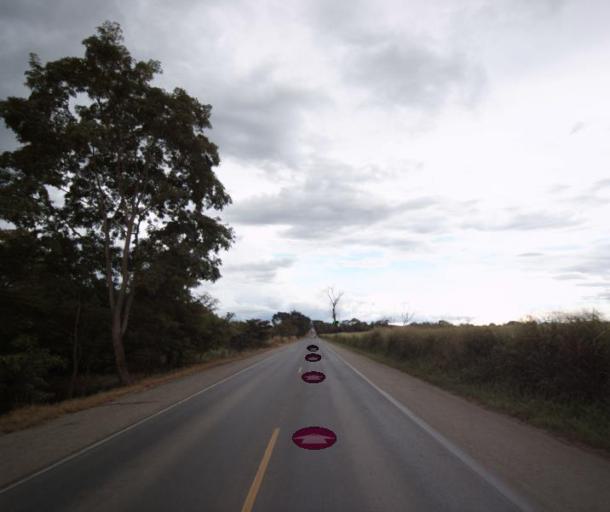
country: BR
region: Goias
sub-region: Itapaci
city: Itapaci
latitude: -14.9772
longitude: -49.3950
